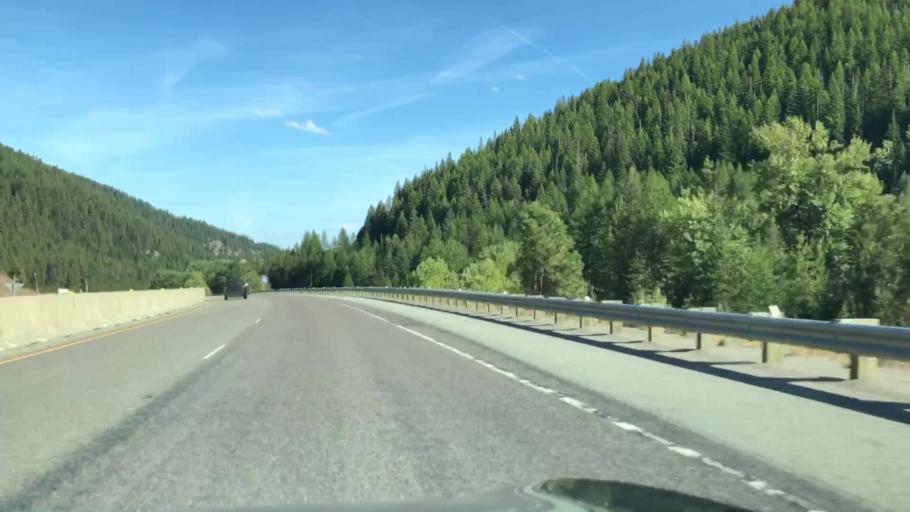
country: US
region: Montana
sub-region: Sanders County
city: Thompson Falls
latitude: 47.4077
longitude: -115.5040
